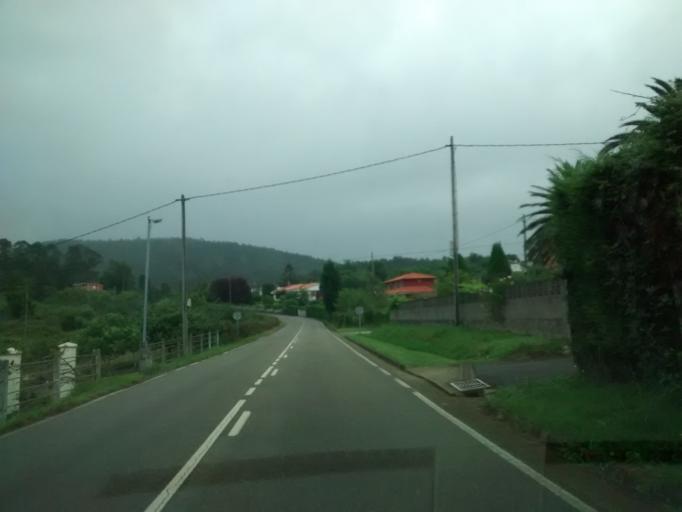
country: ES
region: Asturias
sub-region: Province of Asturias
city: Villaviciosa
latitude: 43.5277
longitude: -5.3737
